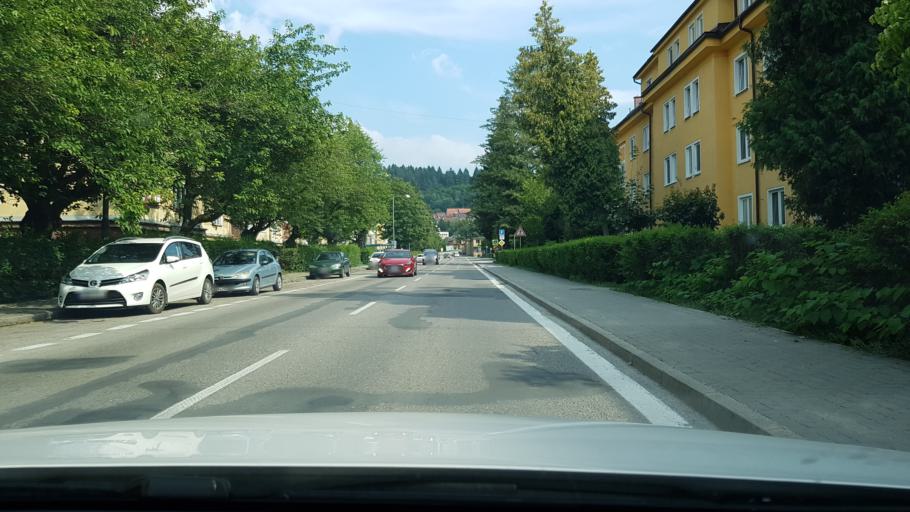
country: SK
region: Trenciansky
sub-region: Okres Povazska Bystrica
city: Povazska Bystrica
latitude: 49.1087
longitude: 18.4575
